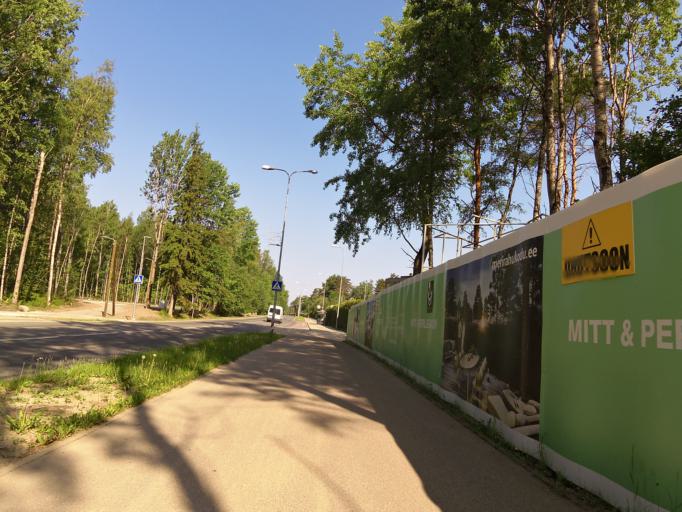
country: EE
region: Harju
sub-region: Saue vald
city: Laagri
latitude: 59.4395
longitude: 24.6242
